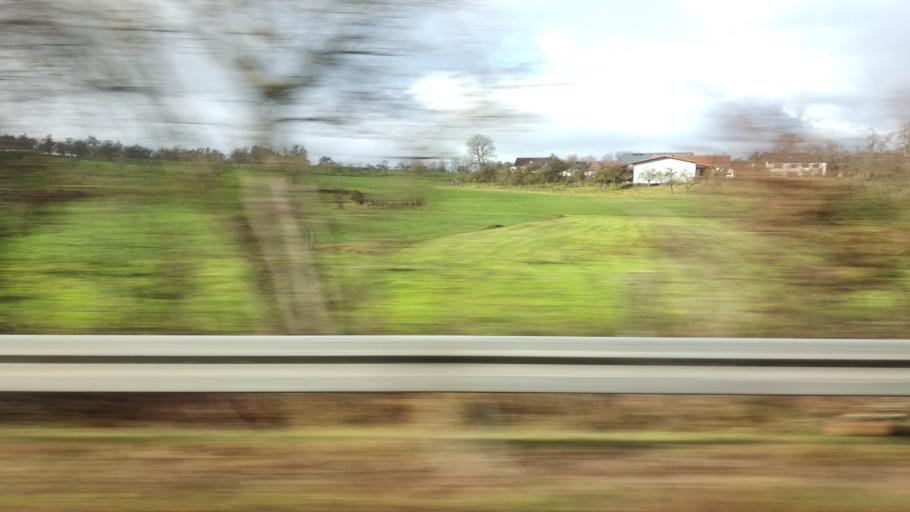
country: DE
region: Bavaria
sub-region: Swabia
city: Weissensberg
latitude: 47.6272
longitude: 9.7400
